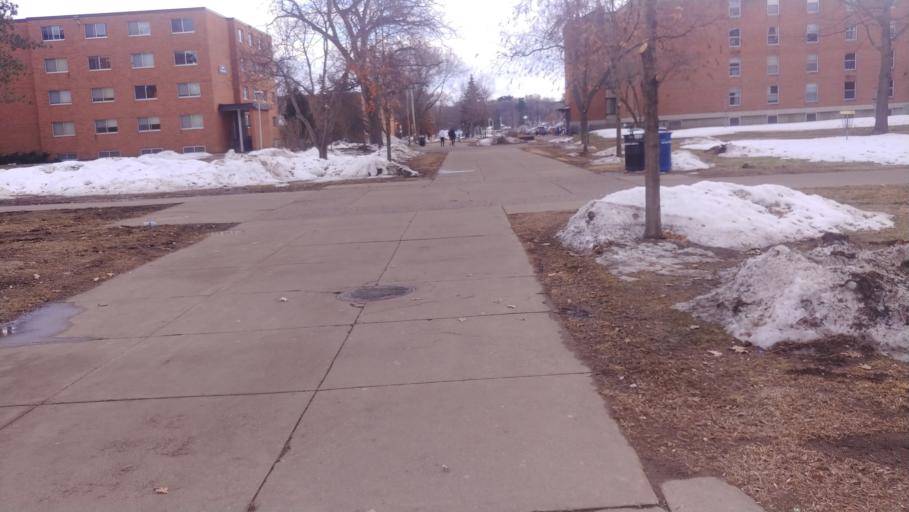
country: US
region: Wisconsin
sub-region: Dunn County
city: Menomonie
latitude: 44.8725
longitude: -91.9284
